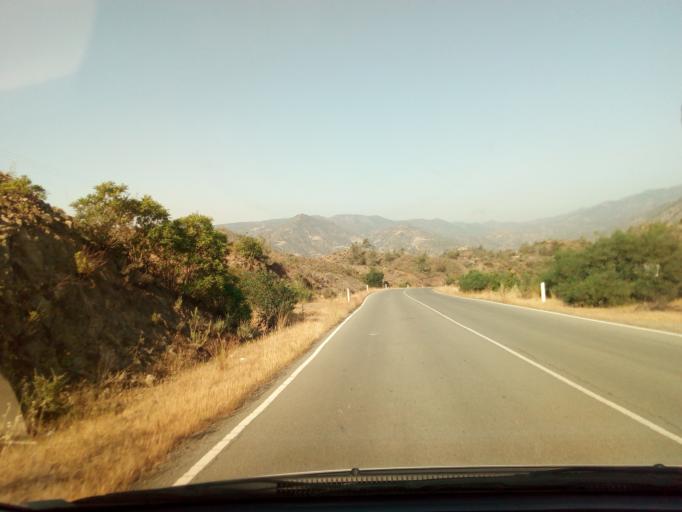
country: CY
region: Limassol
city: Parekklisha
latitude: 34.8434
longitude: 33.1386
